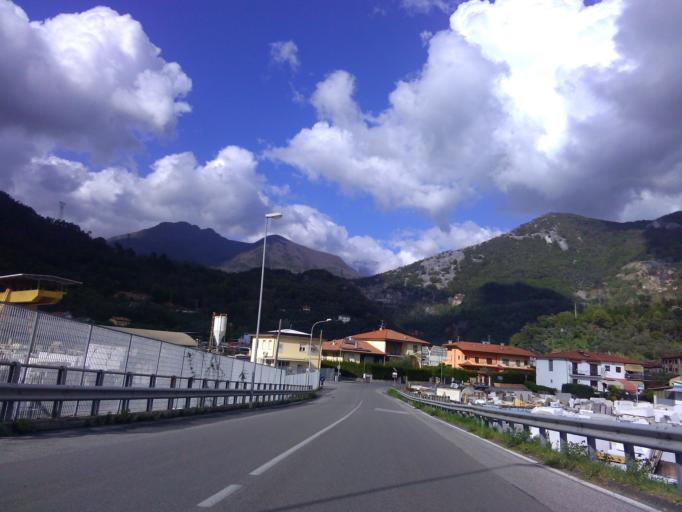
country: IT
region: Tuscany
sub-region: Provincia di Lucca
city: Ripa-Pozzi-Querceta-Ponterosso
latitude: 43.9819
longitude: 10.2164
